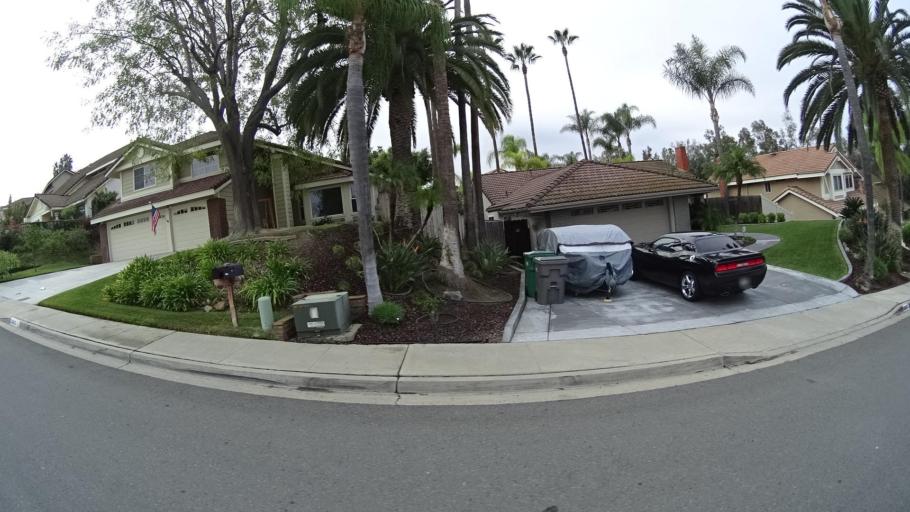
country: US
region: California
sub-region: San Diego County
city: Rancho San Diego
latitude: 32.7533
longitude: -116.9153
